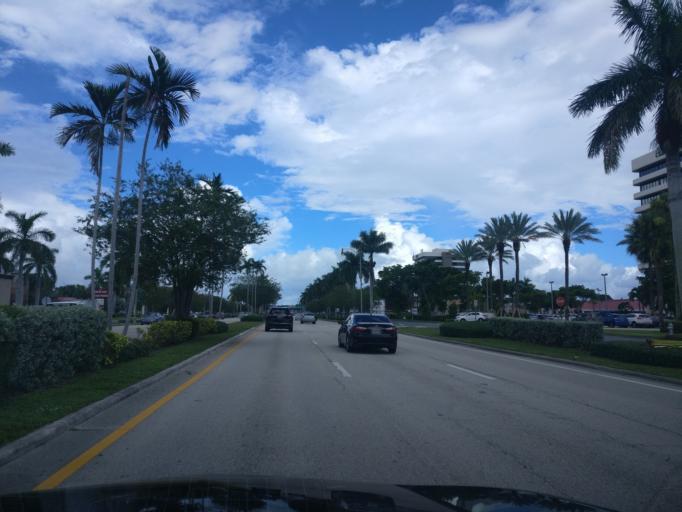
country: US
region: Florida
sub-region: Palm Beach County
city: Schall Circle
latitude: 26.7134
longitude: -80.0945
